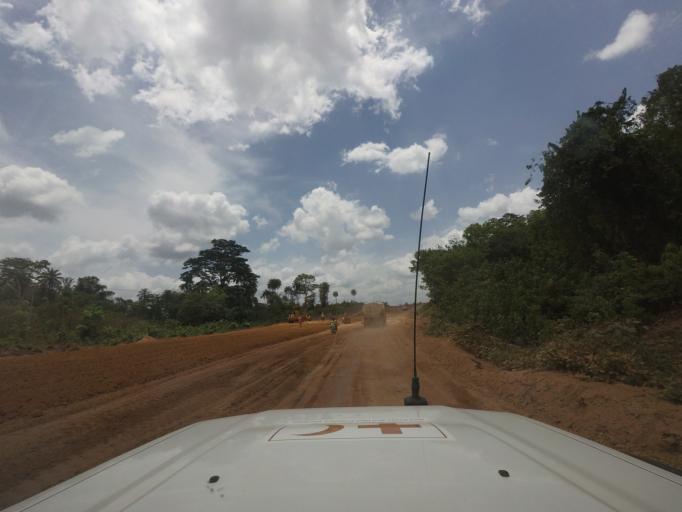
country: LR
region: Nimba
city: Sanniquellie
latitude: 7.2462
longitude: -8.8639
